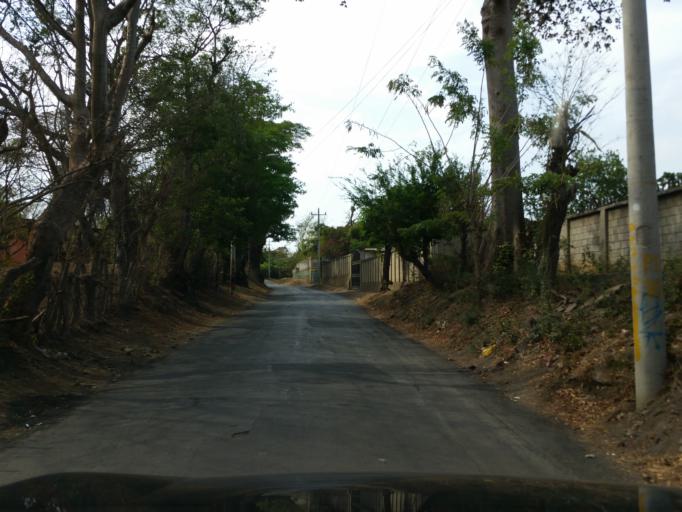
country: NI
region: Masaya
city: Ticuantepe
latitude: 12.0775
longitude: -86.2166
